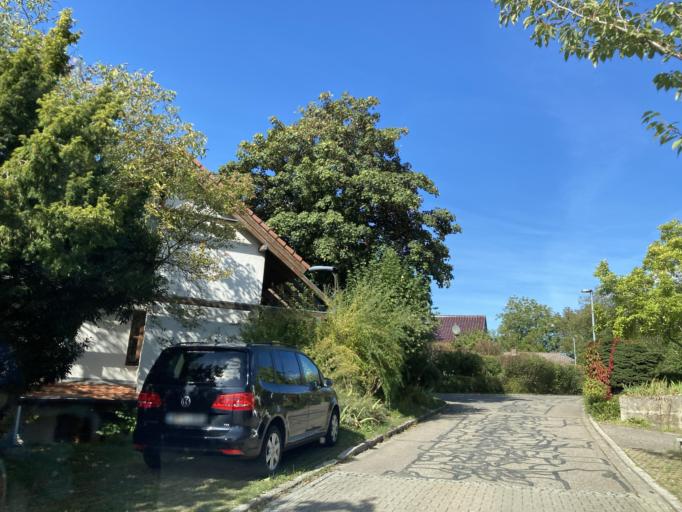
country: DE
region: Baden-Wuerttemberg
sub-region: Freiburg Region
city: Mullheim
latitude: 47.8162
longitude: 7.6290
